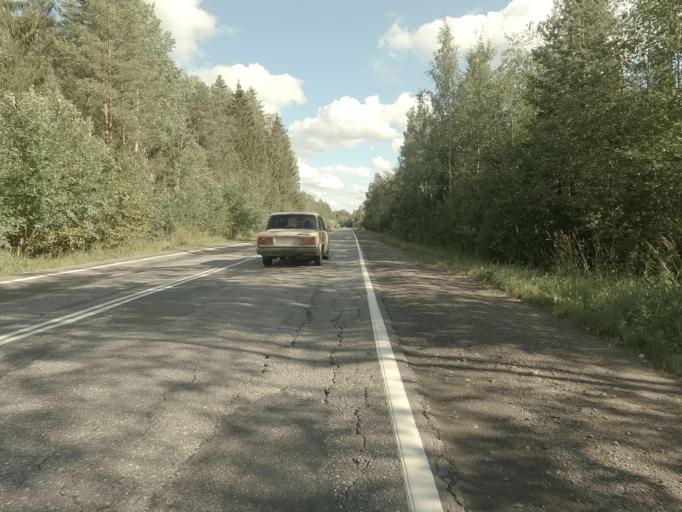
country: RU
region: Leningrad
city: Borisova Griva
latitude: 59.9896
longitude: 30.8850
